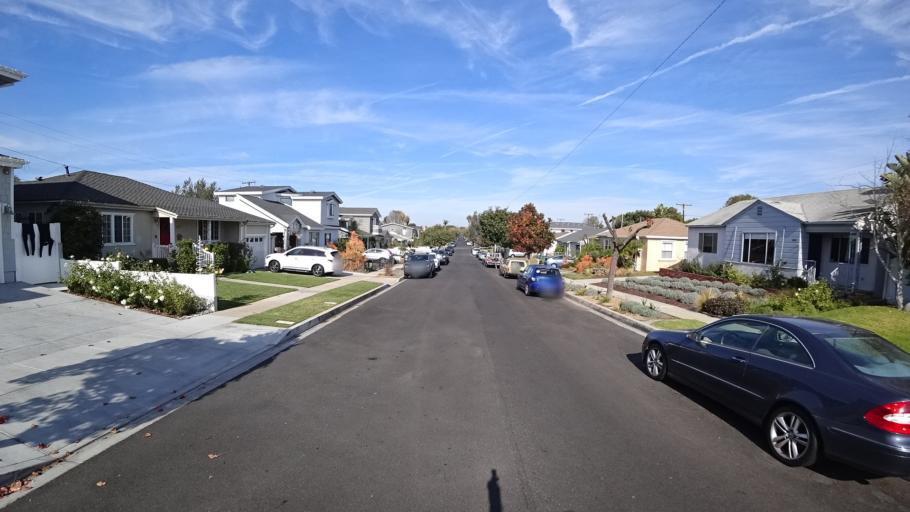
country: US
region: California
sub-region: Los Angeles County
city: Lawndale
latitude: 33.8882
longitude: -118.3817
